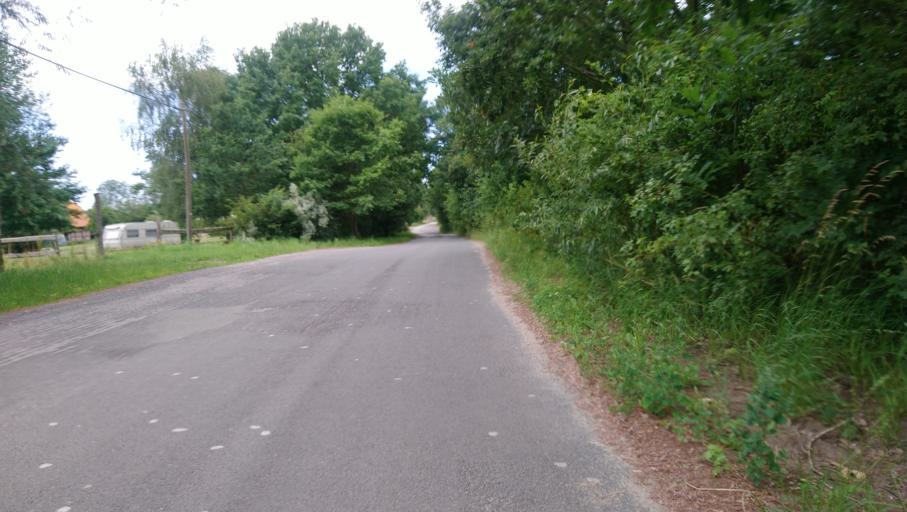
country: DE
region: Mecklenburg-Vorpommern
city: Elmenhorst
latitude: 54.1720
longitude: 12.0148
